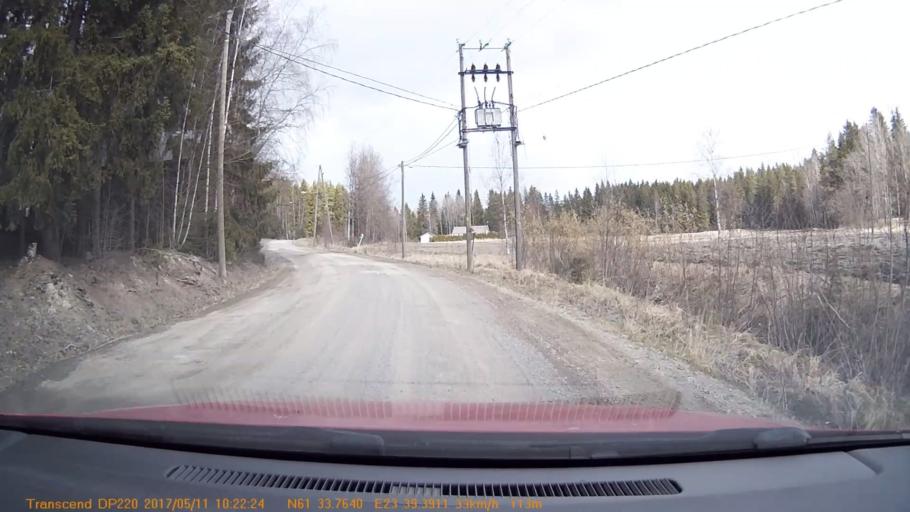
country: FI
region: Pirkanmaa
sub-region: Tampere
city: Yloejaervi
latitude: 61.5626
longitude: 23.6563
